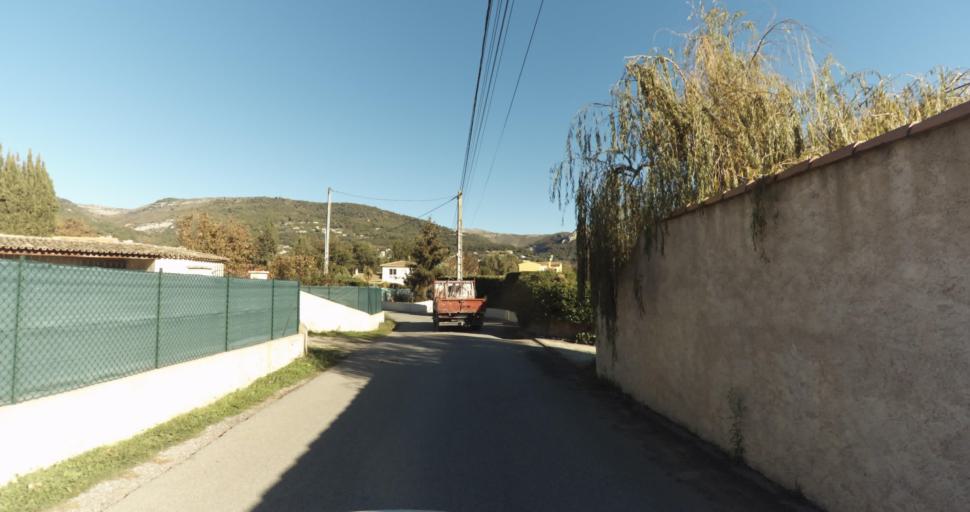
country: FR
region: Provence-Alpes-Cote d'Azur
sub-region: Departement des Alpes-Maritimes
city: Vence
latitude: 43.7166
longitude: 7.0876
